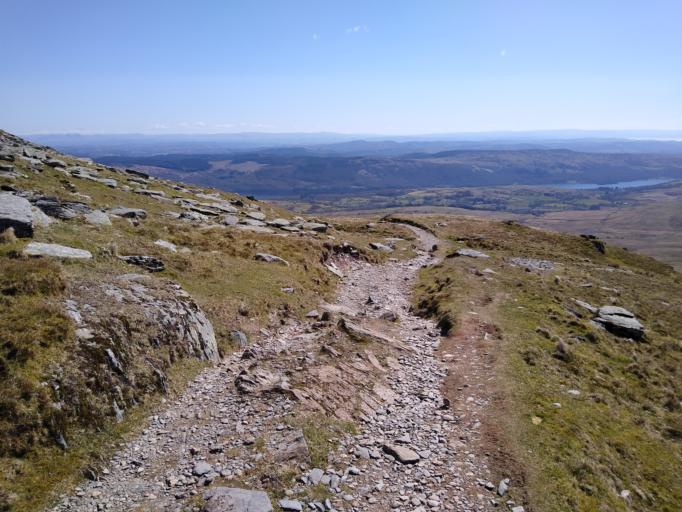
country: GB
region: England
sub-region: Cumbria
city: Ulverston
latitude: 54.3577
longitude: -3.1400
